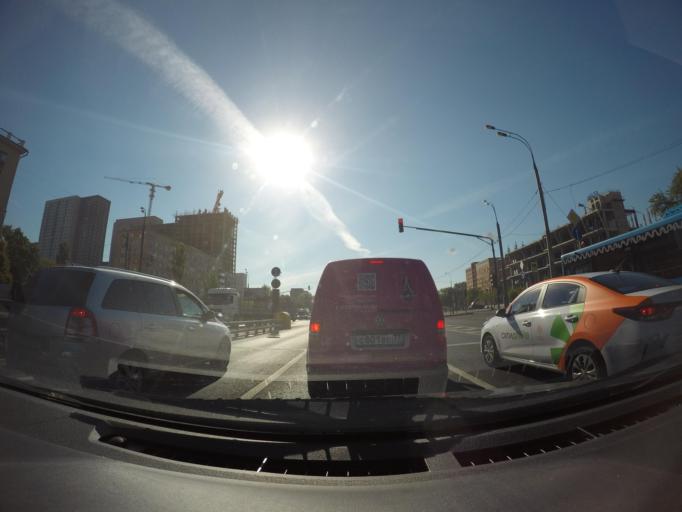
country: RU
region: Moscow
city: Ryazanskiy
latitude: 55.7232
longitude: 37.7688
